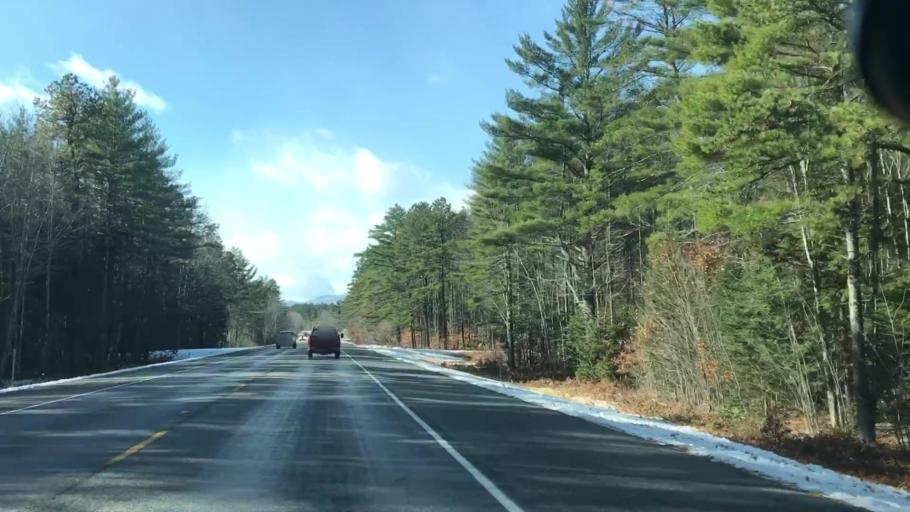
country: US
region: New Hampshire
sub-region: Carroll County
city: Freedom
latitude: 43.7904
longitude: -71.0807
